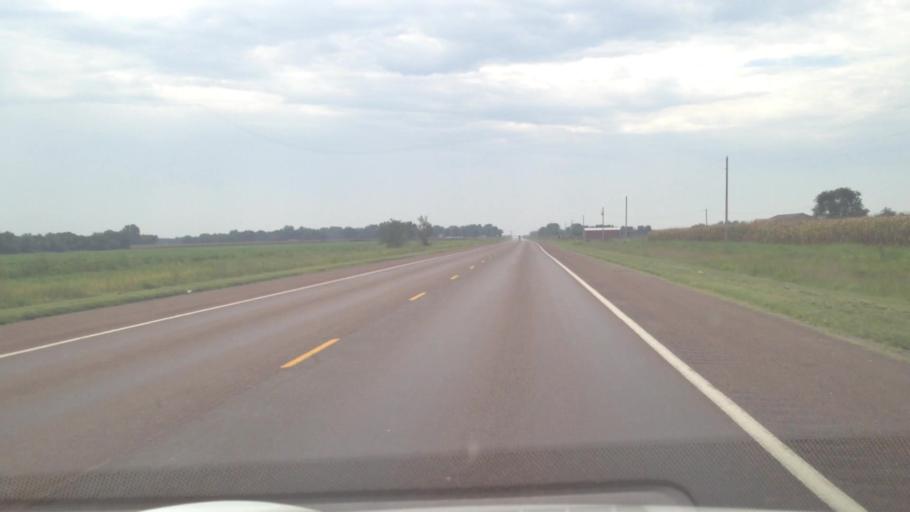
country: US
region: Kansas
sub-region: Crawford County
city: Girard
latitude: 37.4509
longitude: -94.8331
